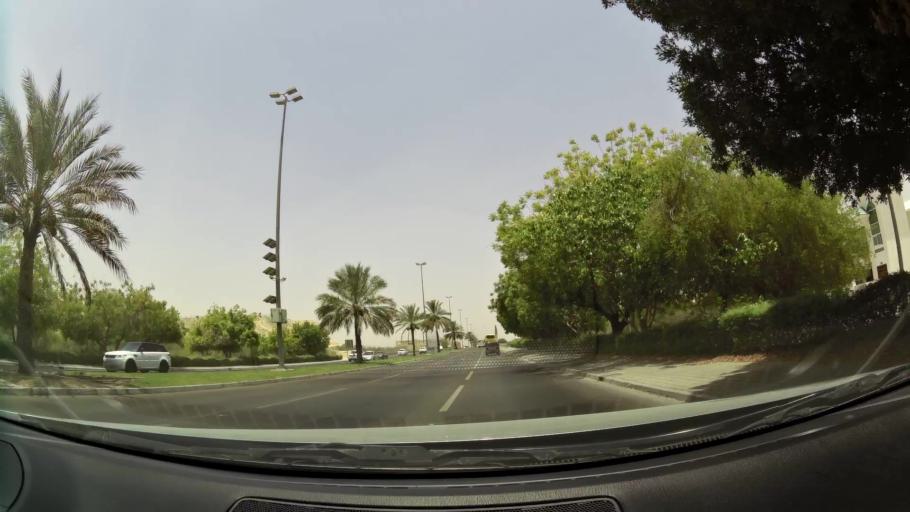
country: AE
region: Abu Dhabi
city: Al Ain
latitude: 24.2059
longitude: 55.7716
